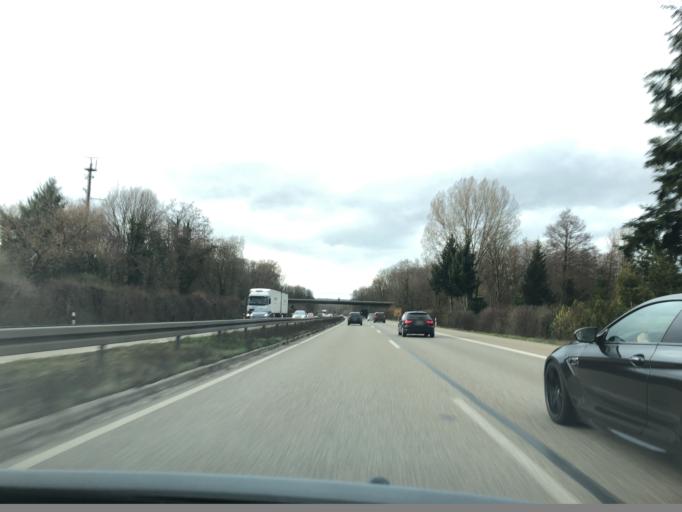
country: DE
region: Baden-Wuerttemberg
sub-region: Freiburg Region
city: Umkirch
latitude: 48.0140
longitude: 7.7964
